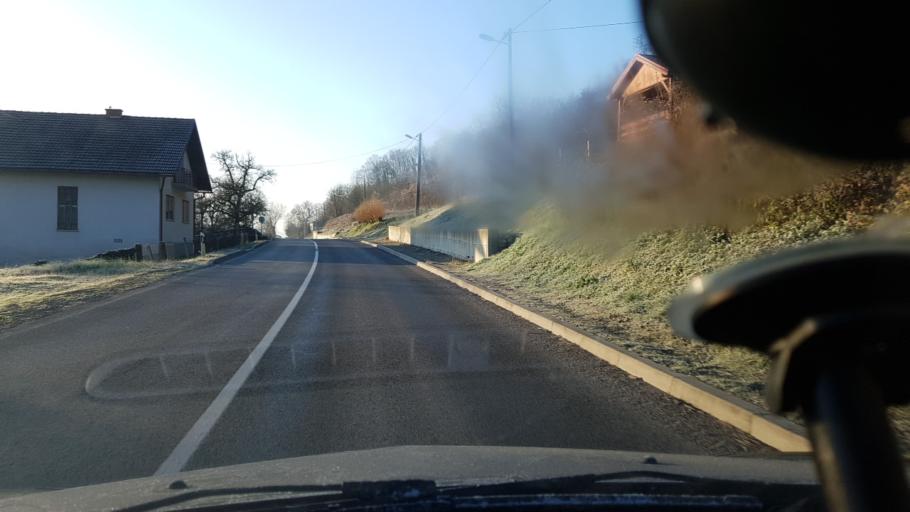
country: HR
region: Krapinsko-Zagorska
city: Zabok
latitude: 46.0162
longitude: 15.8537
